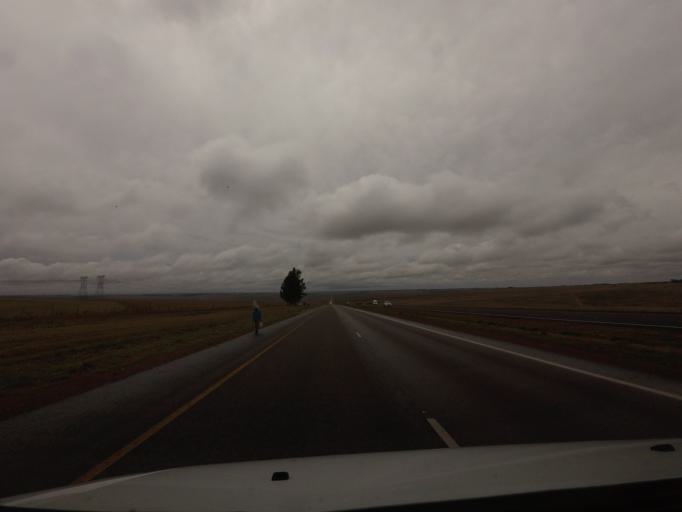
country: ZA
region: Mpumalanga
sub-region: Nkangala District Municipality
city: Middelburg
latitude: -25.8263
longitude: 29.5538
